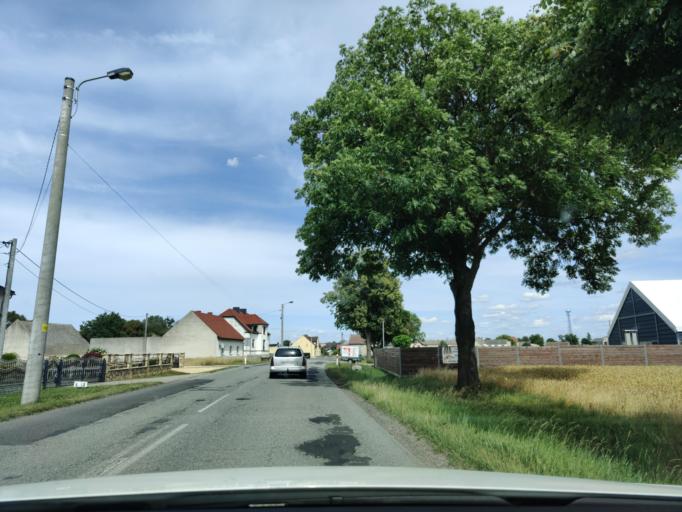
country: PL
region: Opole Voivodeship
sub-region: Powiat krapkowicki
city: Strzeleczki
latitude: 50.4548
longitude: 17.8419
